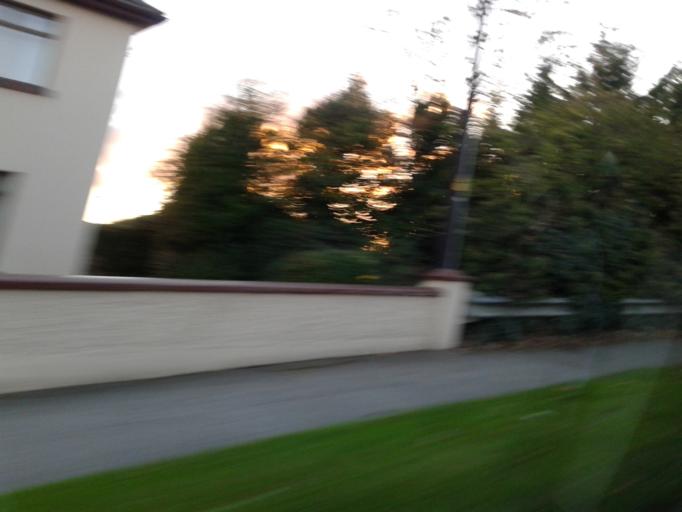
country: IE
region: Leinster
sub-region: Lu
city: Drogheda
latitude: 53.7193
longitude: -6.3744
